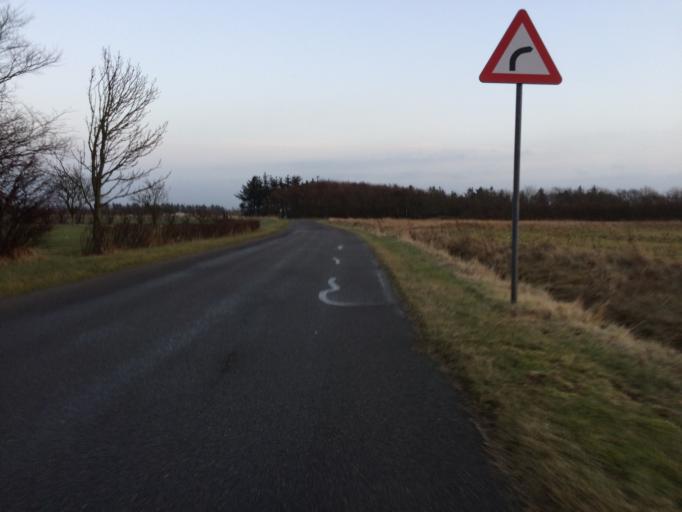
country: DK
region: Central Jutland
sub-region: Holstebro Kommune
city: Ulfborg
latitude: 56.2775
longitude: 8.2888
